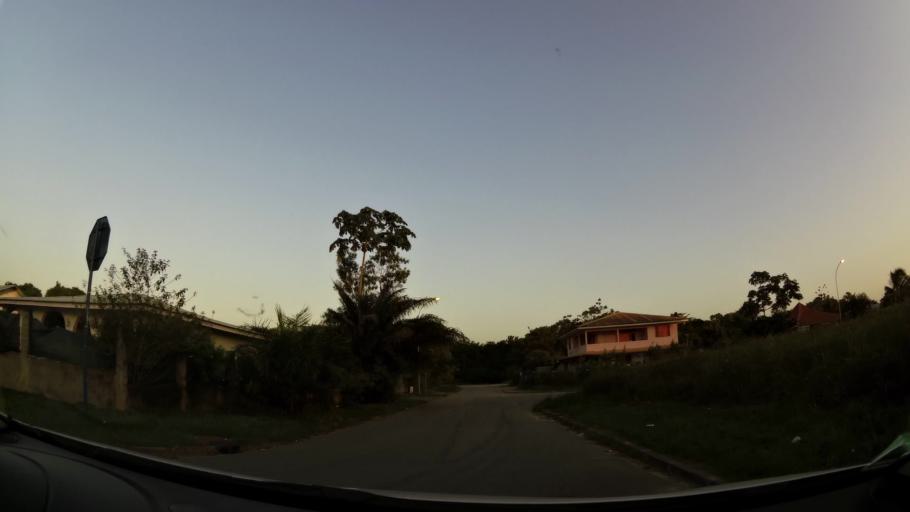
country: GF
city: Macouria
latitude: 4.9298
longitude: -52.4044
